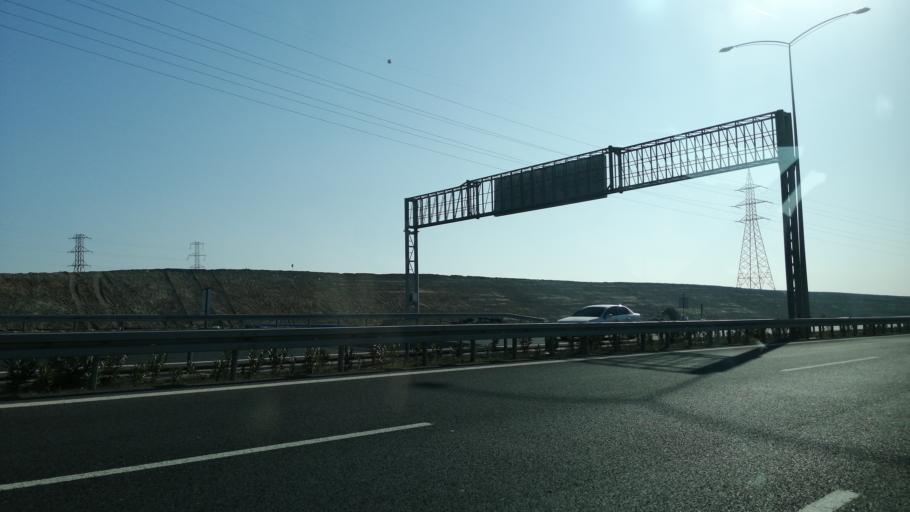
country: TR
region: Kocaeli
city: Tavsanli
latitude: 40.7921
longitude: 29.5128
